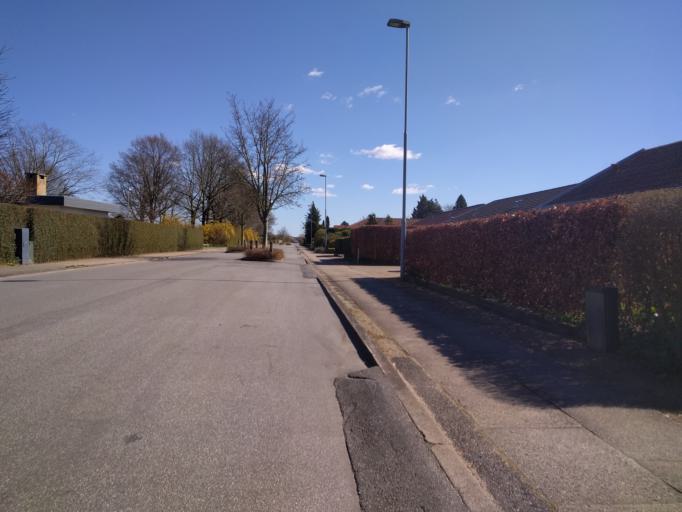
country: DK
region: South Denmark
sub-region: Kerteminde Kommune
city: Langeskov
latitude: 55.3636
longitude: 10.5896
